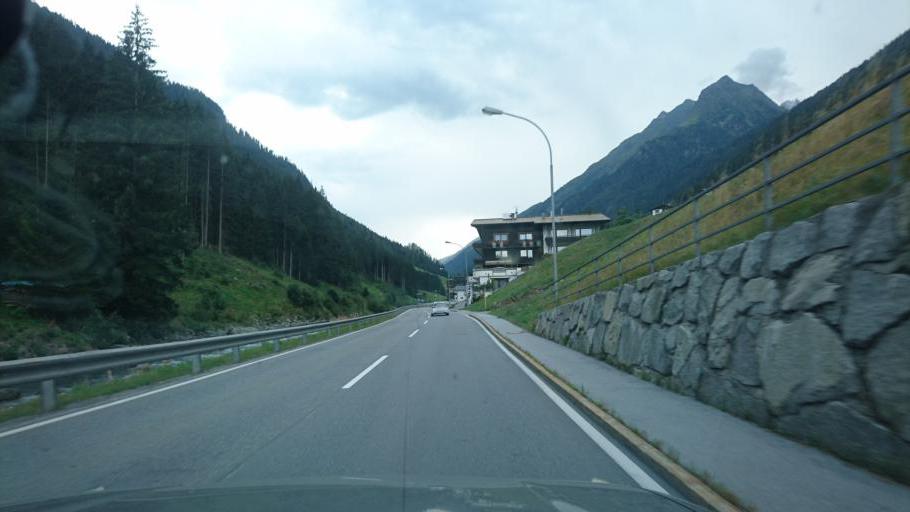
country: AT
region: Tyrol
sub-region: Politischer Bezirk Landeck
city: Kappl
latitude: 47.0547
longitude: 10.3624
